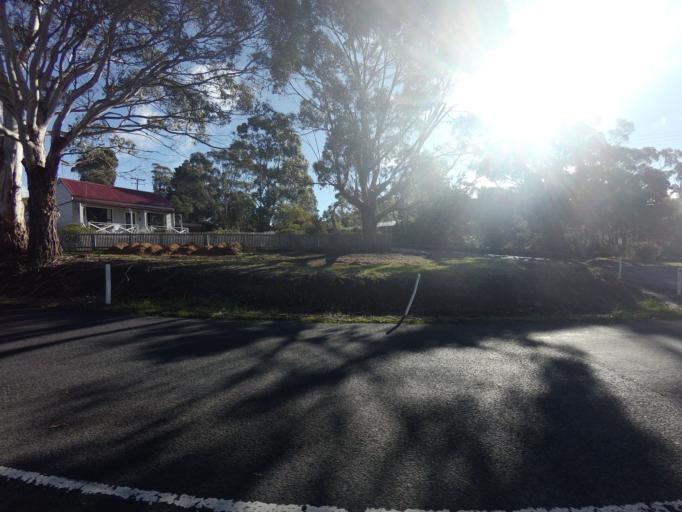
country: AU
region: Tasmania
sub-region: Glenorchy
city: Berriedale
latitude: -42.8245
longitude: 147.2034
